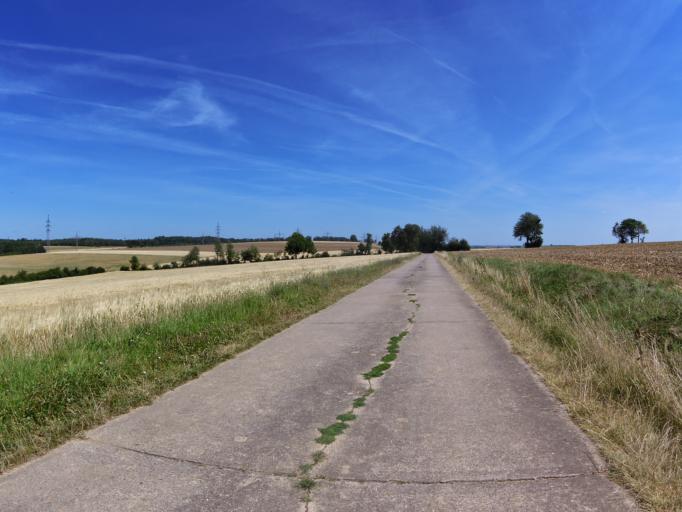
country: DE
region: Bavaria
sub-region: Regierungsbezirk Unterfranken
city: Hettstadt
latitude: 49.8102
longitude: 9.8191
